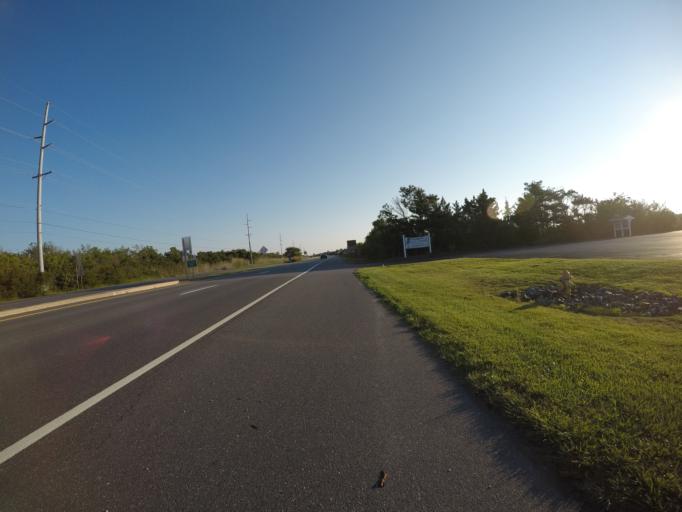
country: US
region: Delaware
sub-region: Sussex County
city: Bethany Beach
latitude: 38.4679
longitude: -75.0516
